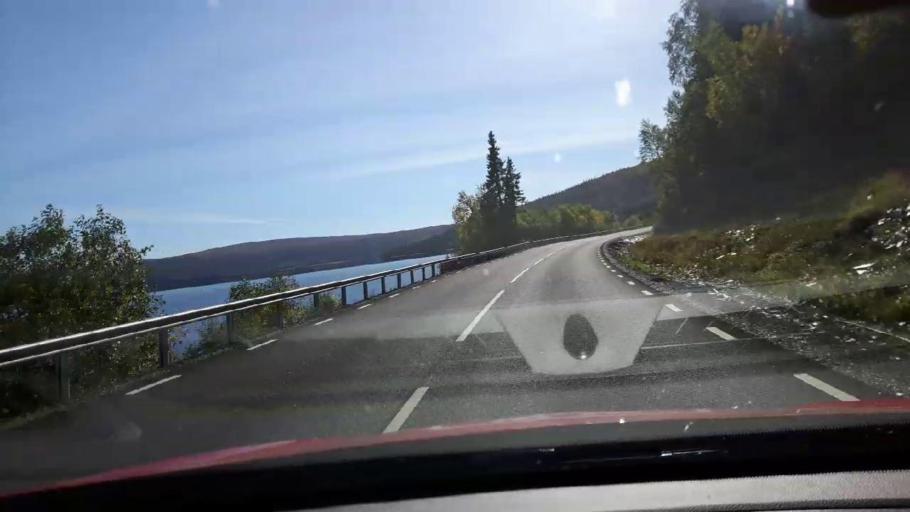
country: NO
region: Nord-Trondelag
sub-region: Royrvik
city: Royrvik
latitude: 64.8262
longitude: 14.0787
